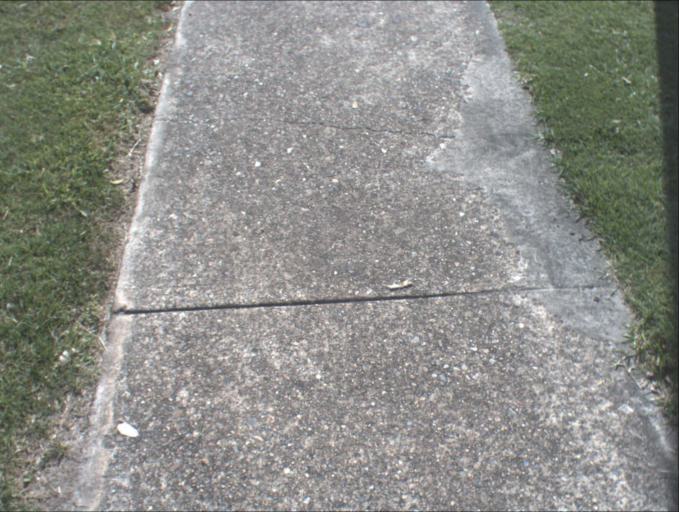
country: AU
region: Queensland
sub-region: Logan
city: Park Ridge South
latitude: -27.6962
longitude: 153.0169
